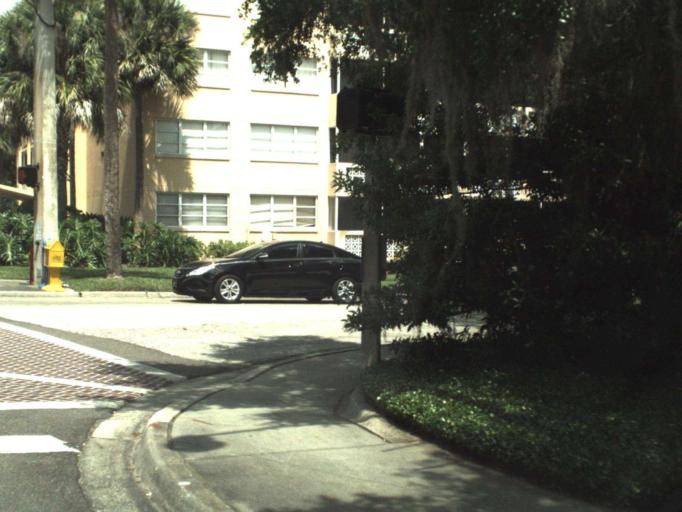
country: US
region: Florida
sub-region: Orange County
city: Winter Park
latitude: 28.5952
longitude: -81.3458
